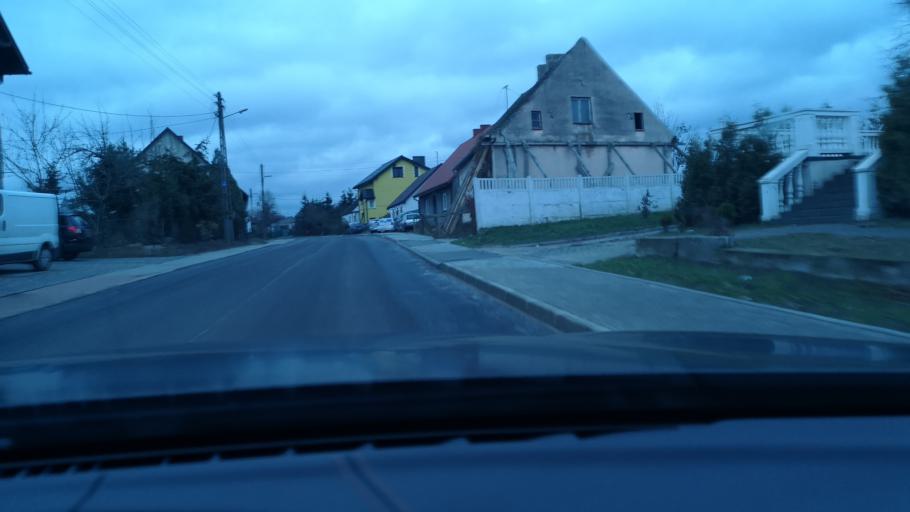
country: PL
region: Greater Poland Voivodeship
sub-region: Powiat slupecki
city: Orchowo
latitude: 52.5986
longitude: 18.0412
